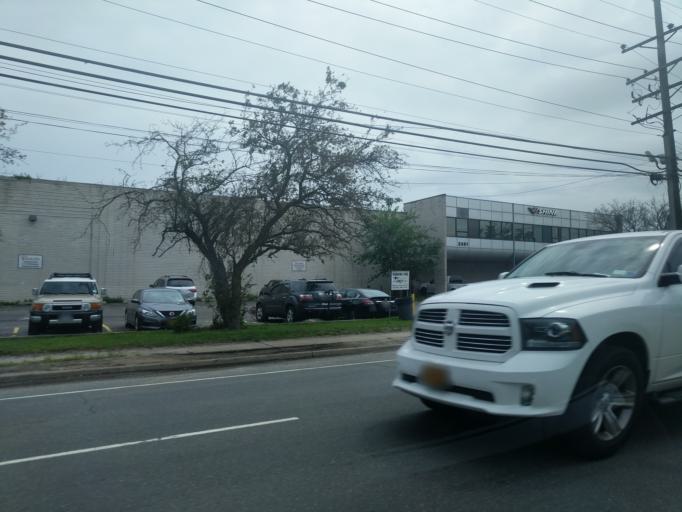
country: US
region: New York
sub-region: Nassau County
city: Oceanside
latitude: 40.6272
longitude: -73.6520
